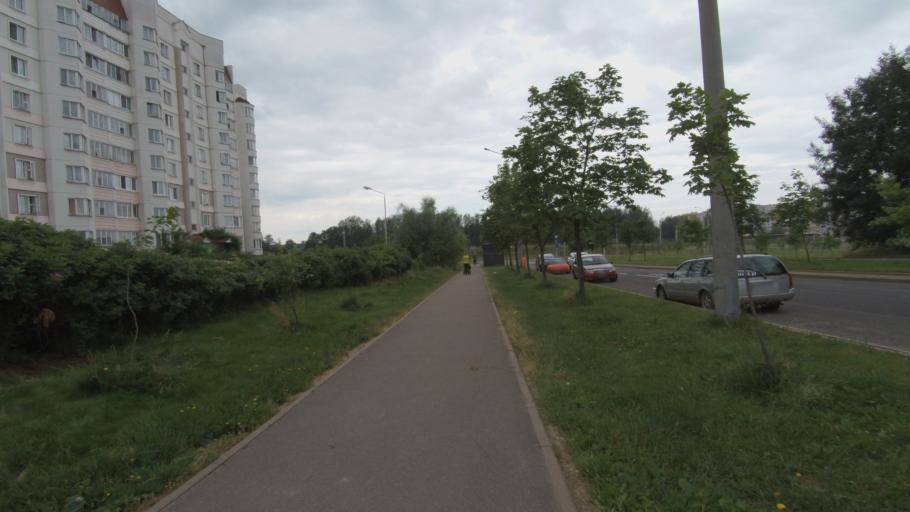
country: BY
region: Minsk
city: Syenitsa
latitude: 53.8494
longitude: 27.5608
